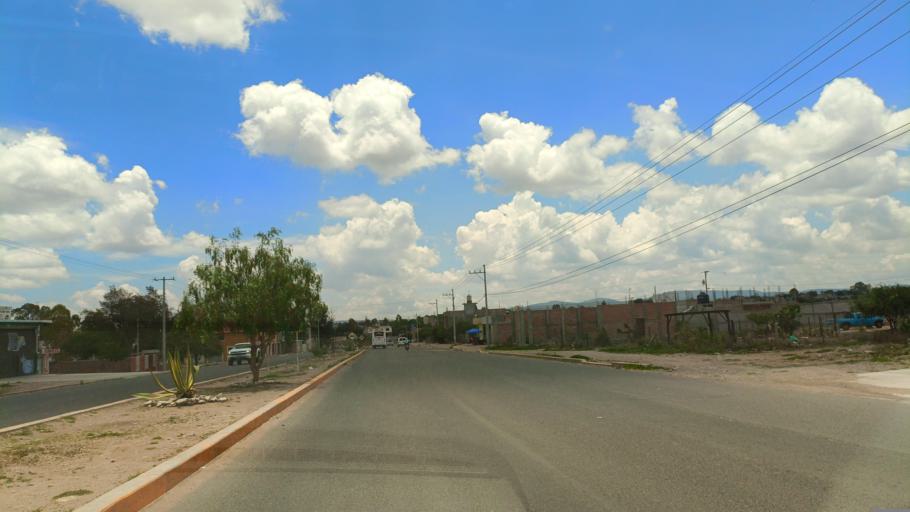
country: MX
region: Guanajuato
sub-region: San Luis de la Paz
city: San Luis de la Paz
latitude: 21.2898
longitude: -100.4950
